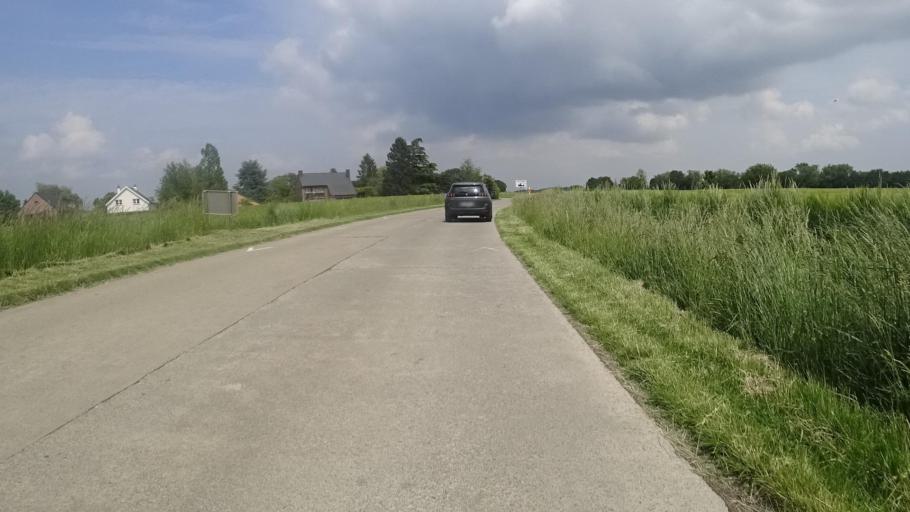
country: BE
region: Wallonia
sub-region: Province du Brabant Wallon
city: Louvain-la-Neuve
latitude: 50.6859
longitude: 4.6415
